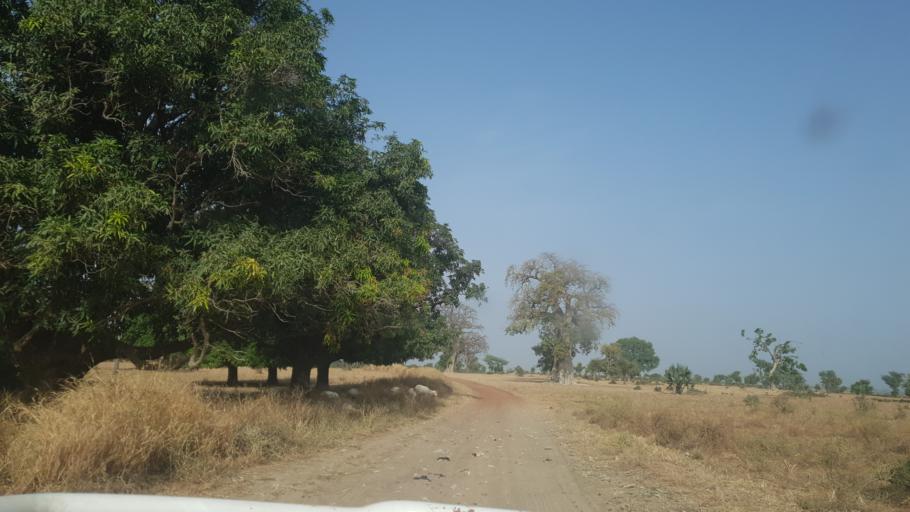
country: ML
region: Segou
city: Baroueli
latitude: 13.3546
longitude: -6.9280
